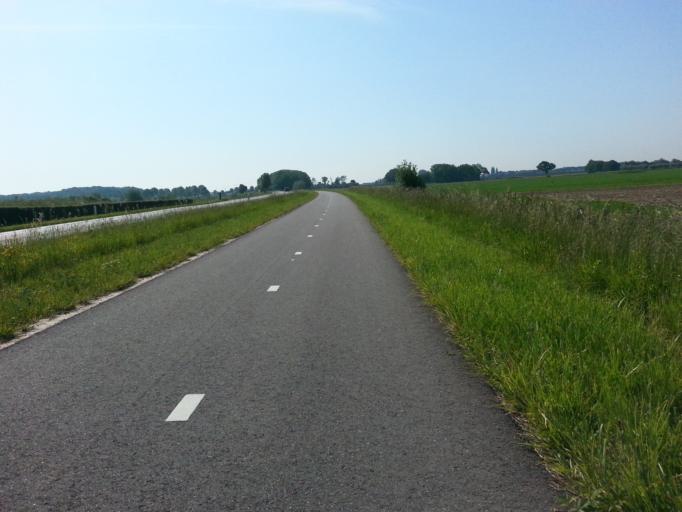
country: NL
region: Utrecht
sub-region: Gemeente Utrechtse Heuvelrug
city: Driebergen-Rijsenburg
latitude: 52.0149
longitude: 5.2648
